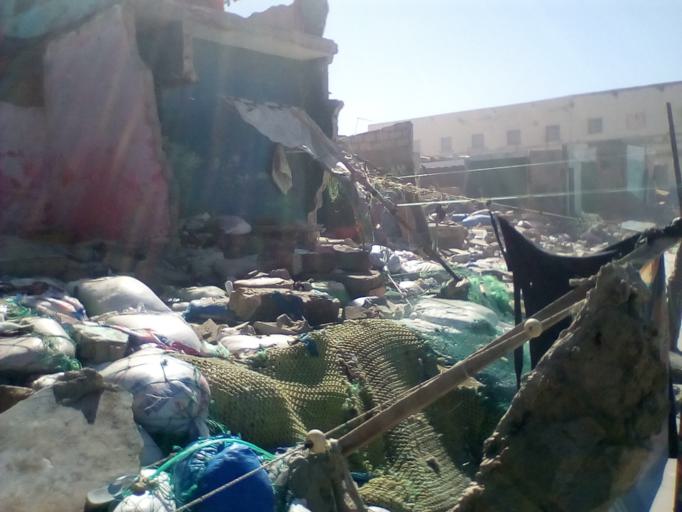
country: SN
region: Saint-Louis
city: Saint-Louis
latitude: 16.0209
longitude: -16.5094
